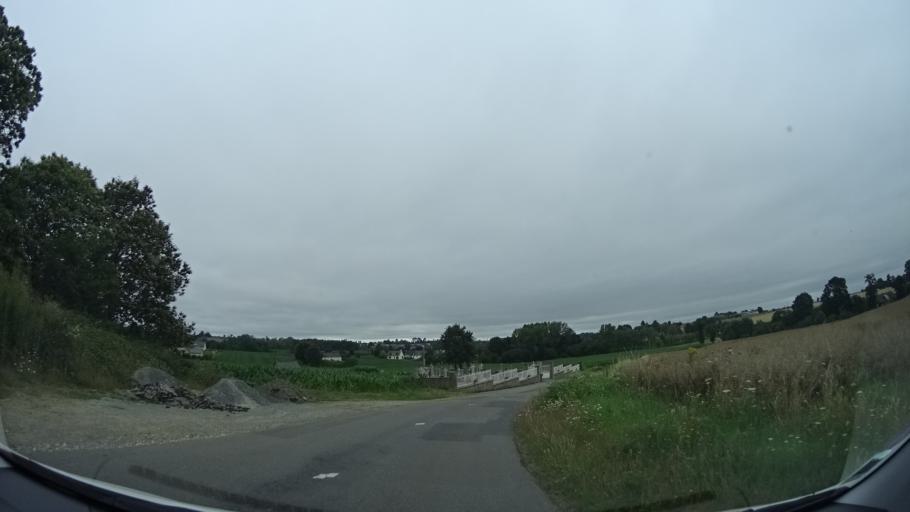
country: FR
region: Brittany
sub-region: Departement d'Ille-et-Vilaine
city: Irodouer
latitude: 48.3052
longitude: -1.9431
